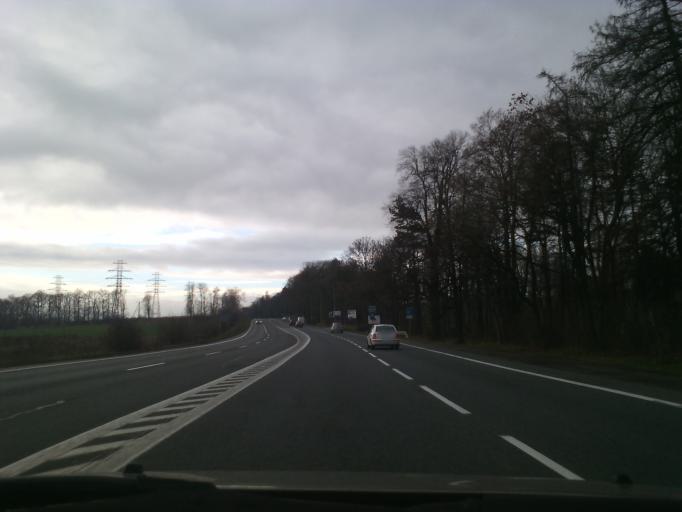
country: PL
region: Lower Silesian Voivodeship
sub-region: Powiat swidnicki
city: Swiebodzice
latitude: 50.8385
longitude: 16.3098
